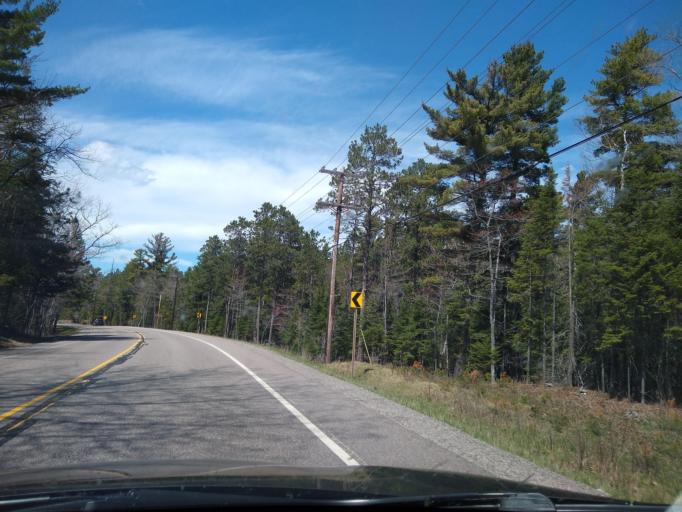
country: US
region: Michigan
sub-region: Marquette County
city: Trowbridge Park
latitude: 46.6309
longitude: -87.4718
